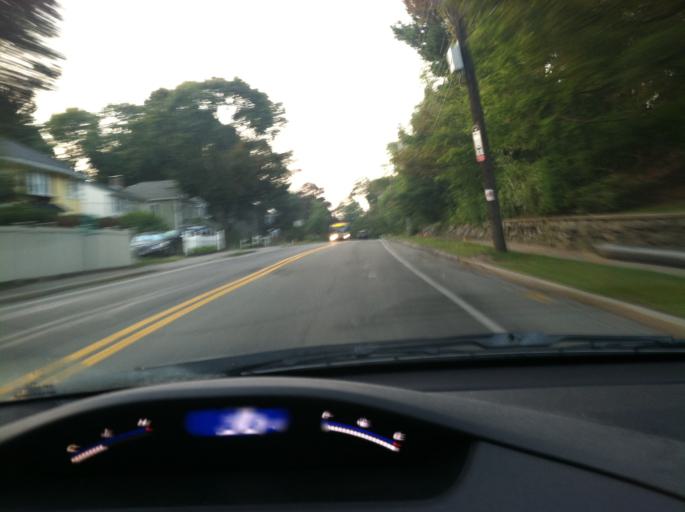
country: US
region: Massachusetts
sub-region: Middlesex County
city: Lexington
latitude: 42.4680
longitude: -71.2434
